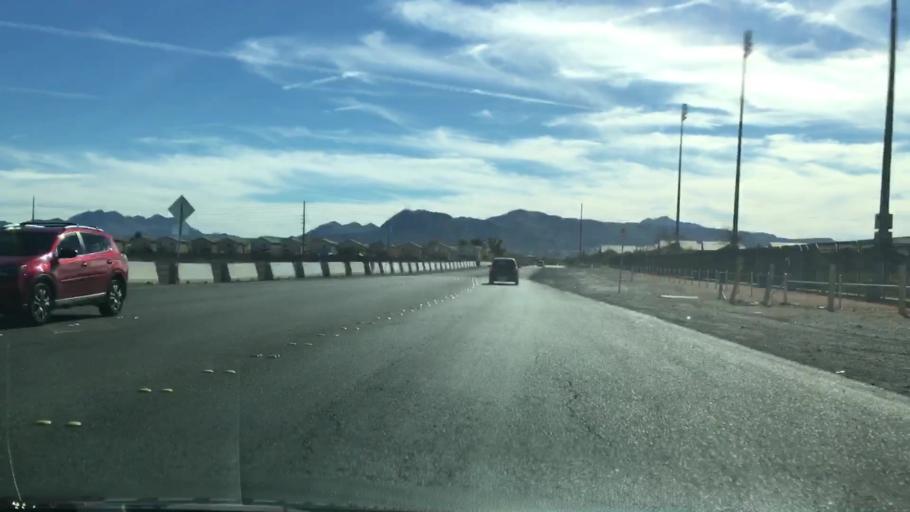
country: US
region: Nevada
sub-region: Clark County
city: Henderson
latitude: 36.0846
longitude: -115.0205
